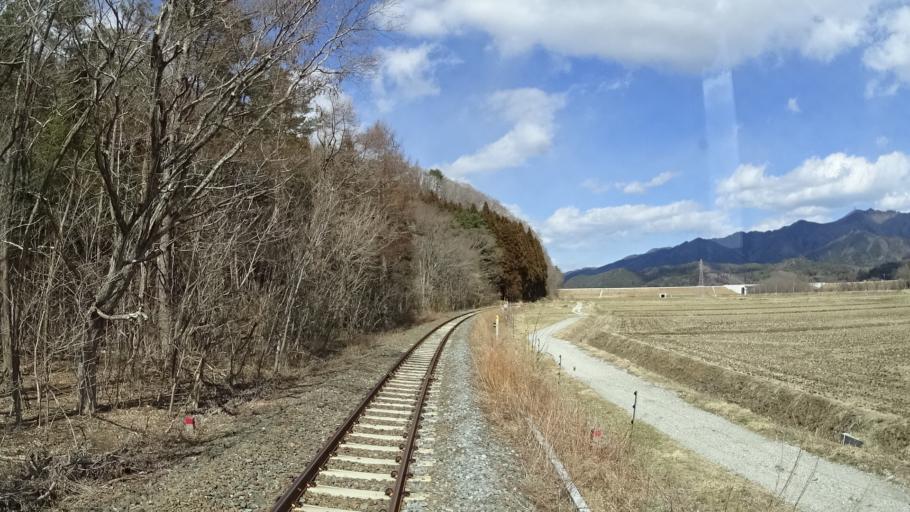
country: JP
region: Iwate
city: Yamada
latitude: 39.5223
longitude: 141.9177
